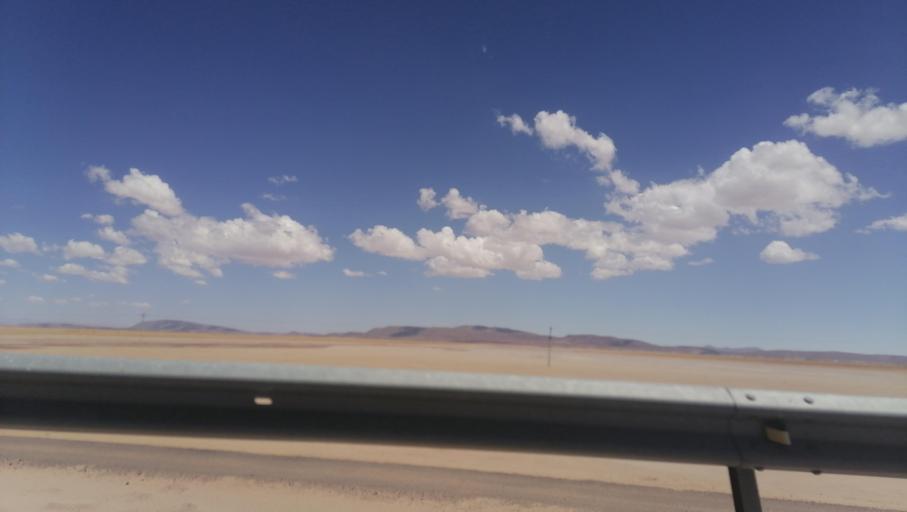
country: BO
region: Oruro
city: Challapata
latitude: -19.2136
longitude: -67.0257
